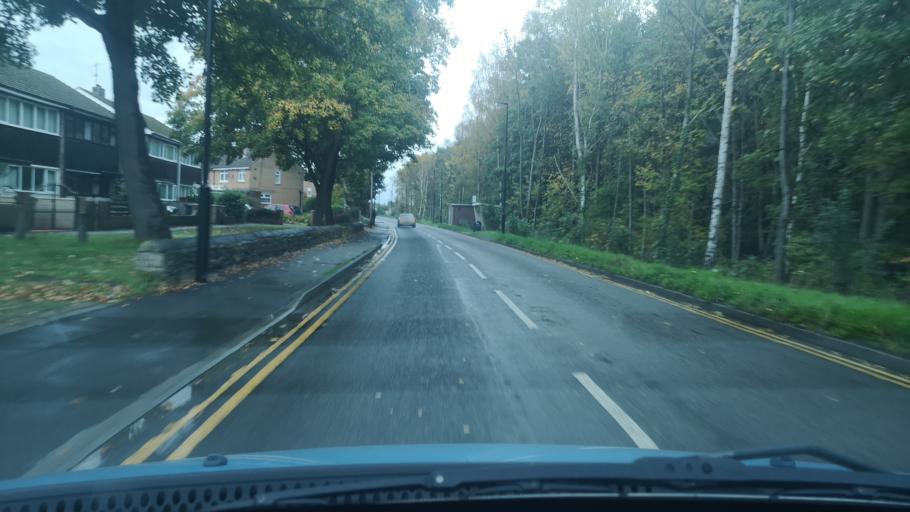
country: GB
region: England
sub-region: Doncaster
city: Campsall
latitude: 53.6216
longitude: -1.1709
